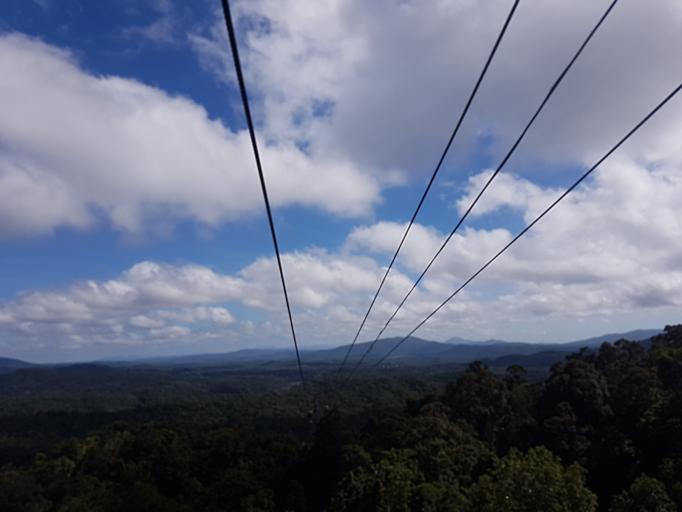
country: AU
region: Queensland
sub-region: Tablelands
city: Kuranda
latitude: -16.8482
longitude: 145.6678
